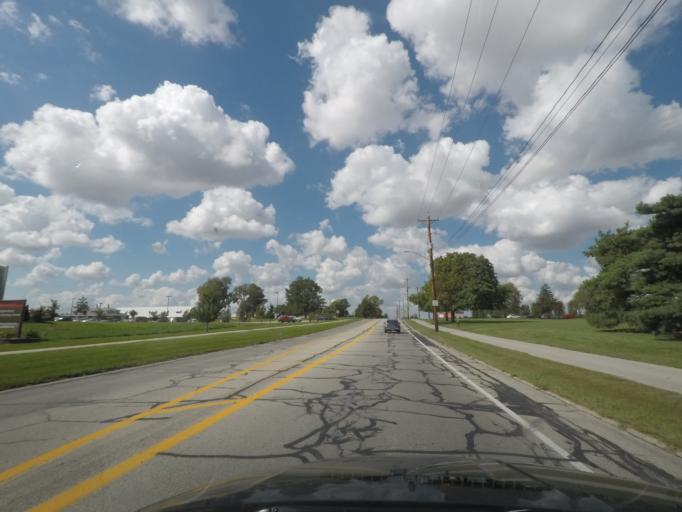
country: US
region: Iowa
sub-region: Story County
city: Ames
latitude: 42.0119
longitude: -93.6500
